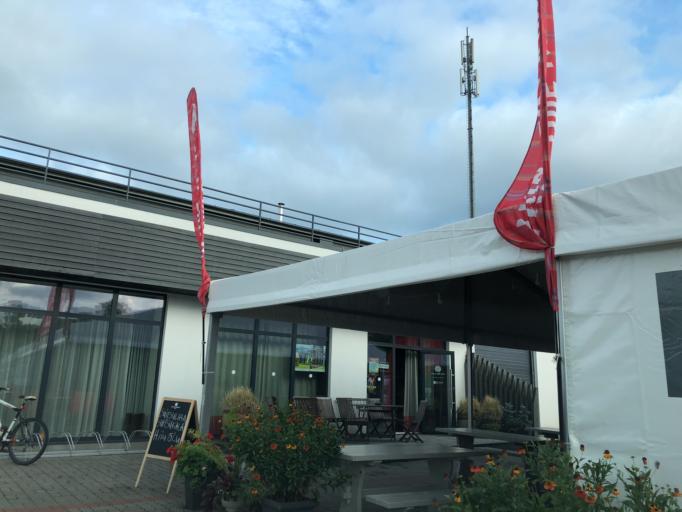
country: EE
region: Hiiumaa
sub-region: Kaerdla linn
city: Kardla
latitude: 58.7878
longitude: 22.8304
